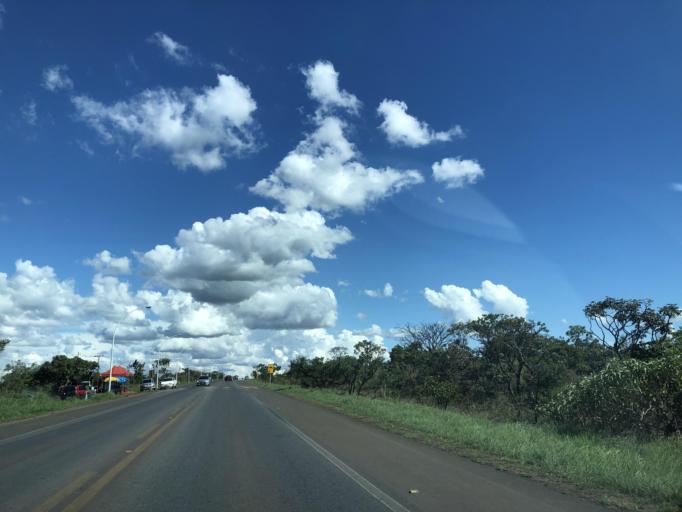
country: BR
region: Federal District
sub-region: Brasilia
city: Brasilia
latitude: -15.6671
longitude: -47.8847
